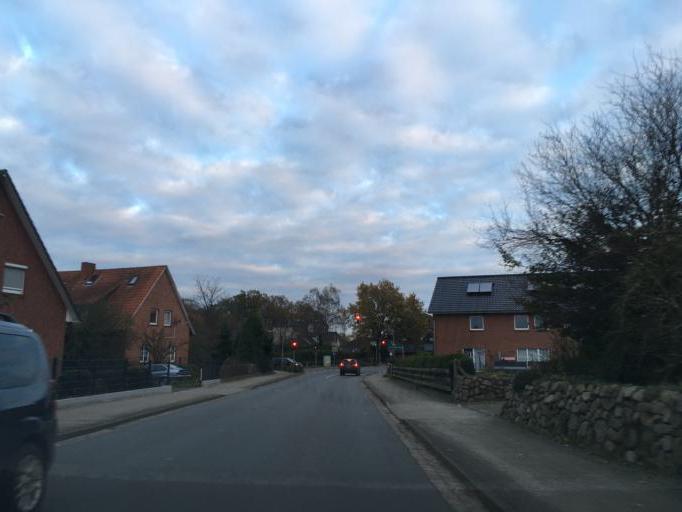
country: DE
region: Lower Saxony
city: Scharnebeck
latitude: 53.2917
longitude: 10.4965
